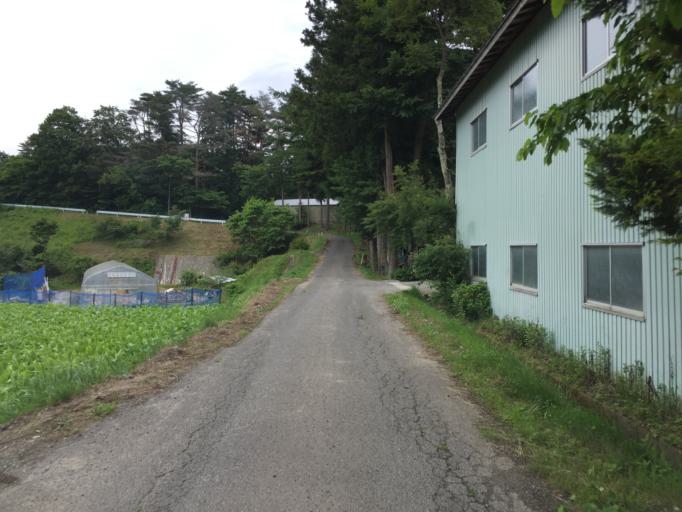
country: JP
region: Fukushima
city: Funehikimachi-funehiki
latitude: 37.4066
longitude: 140.6979
